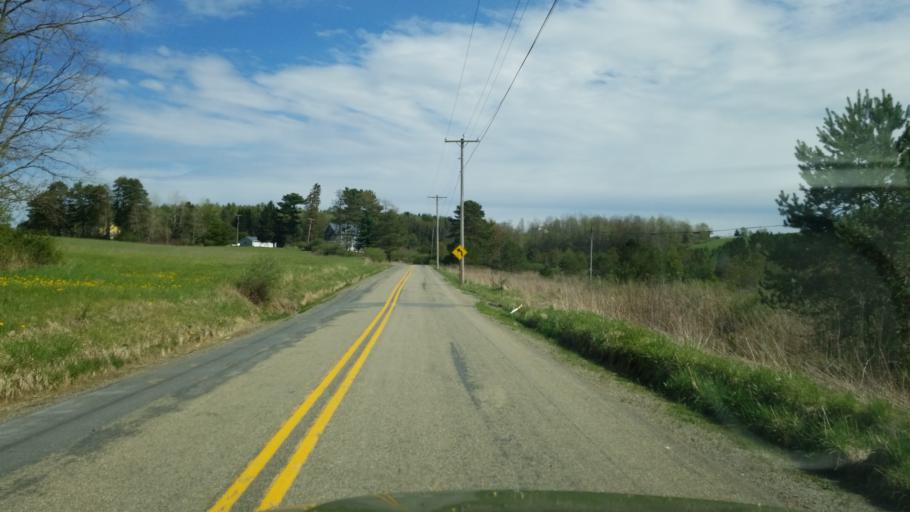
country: US
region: Pennsylvania
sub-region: Jefferson County
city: Brockway
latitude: 41.2225
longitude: -78.8492
